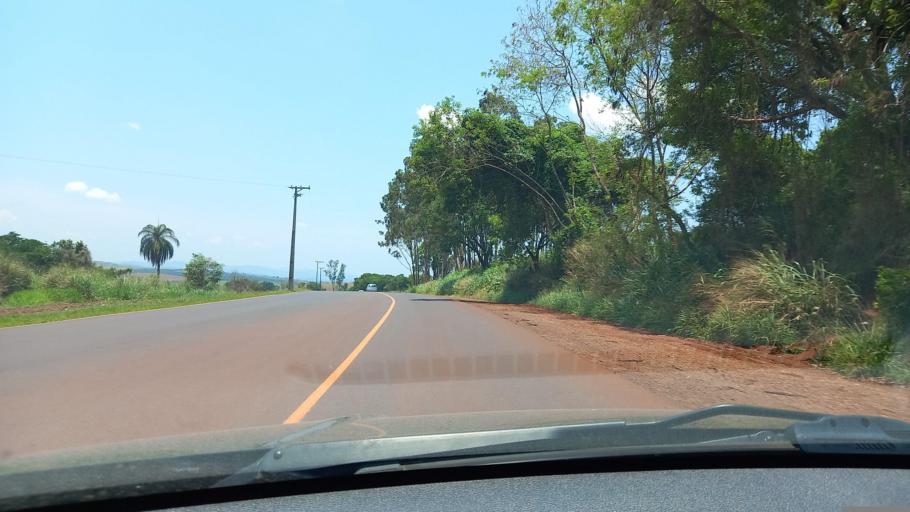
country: BR
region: Sao Paulo
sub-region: Moji-Guacu
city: Mogi-Gaucu
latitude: -22.3429
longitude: -46.8806
